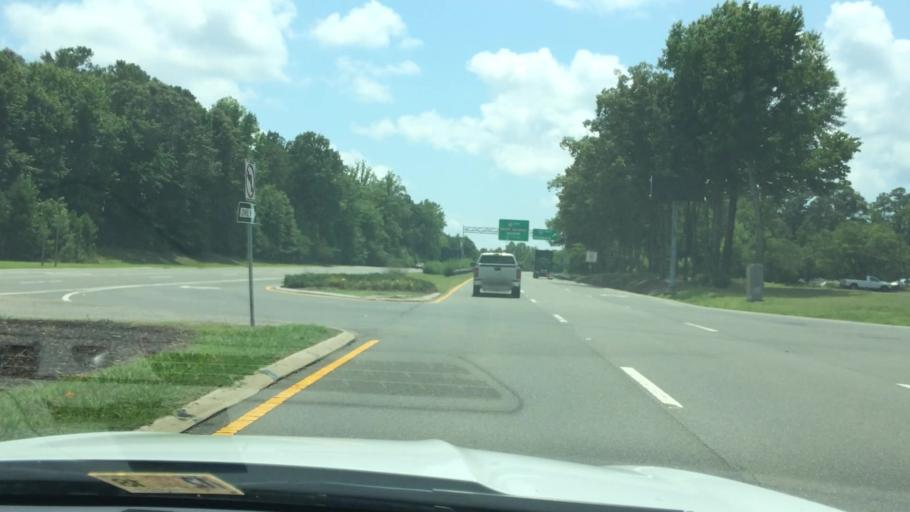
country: US
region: Virginia
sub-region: City of Williamsburg
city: Williamsburg
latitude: 37.2619
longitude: -76.6418
